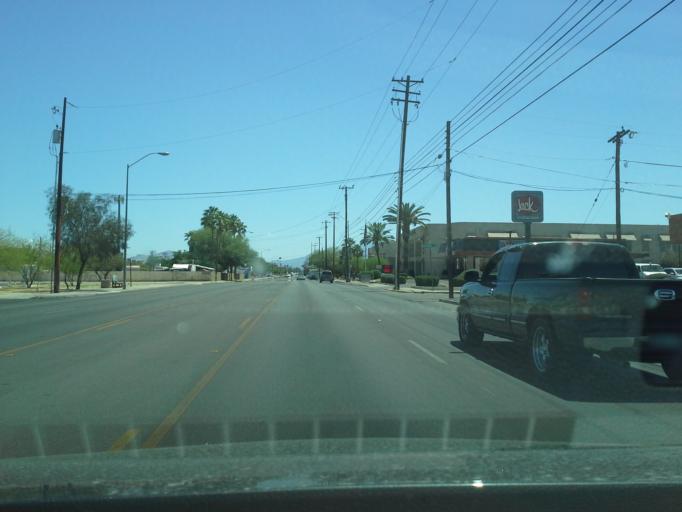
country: US
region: Arizona
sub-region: Pima County
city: Tucson
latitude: 32.2504
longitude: -110.9226
